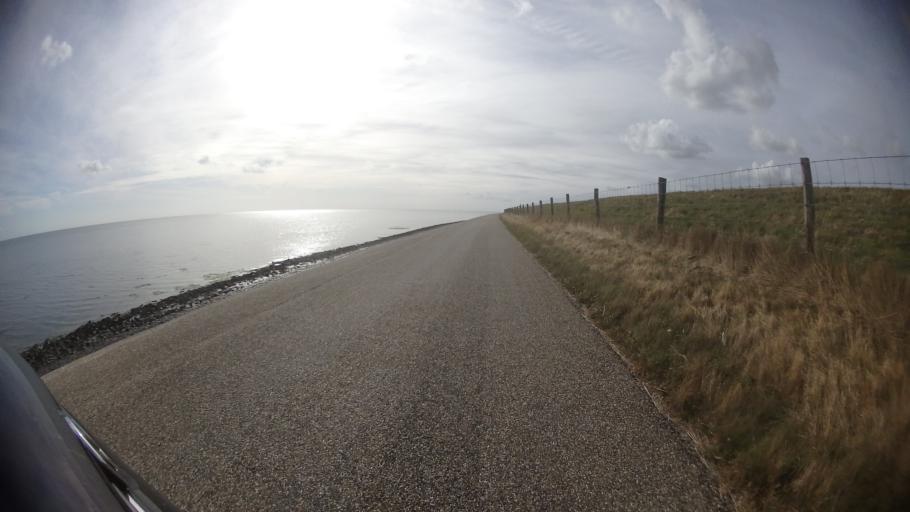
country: NL
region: North Holland
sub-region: Gemeente Texel
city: Den Burg
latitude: 53.0898
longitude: 4.9001
